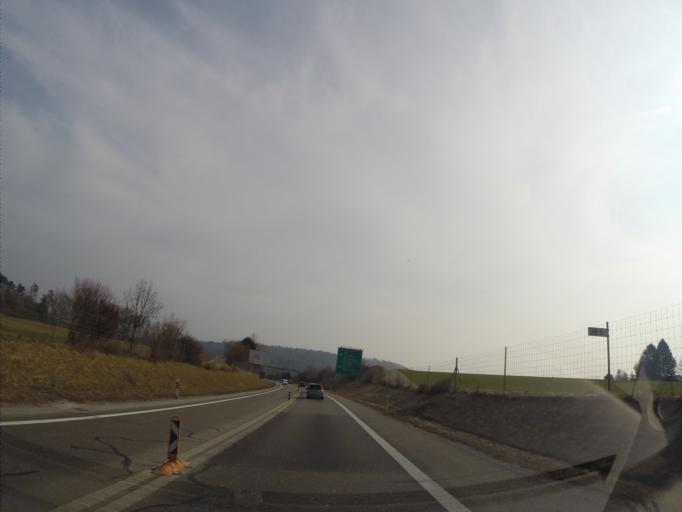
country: CH
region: Zurich
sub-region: Bezirk Winterthur
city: Hettlingen
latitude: 47.5308
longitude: 8.6944
